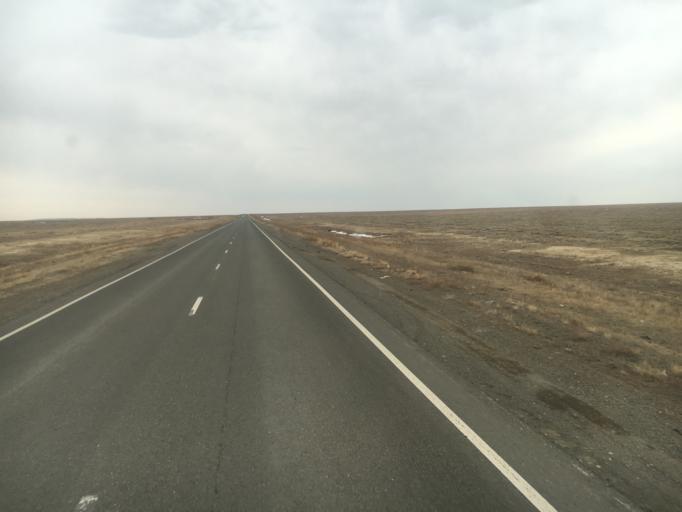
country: KZ
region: Aqtoebe
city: Yrghyz
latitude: 48.7111
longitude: 60.8374
